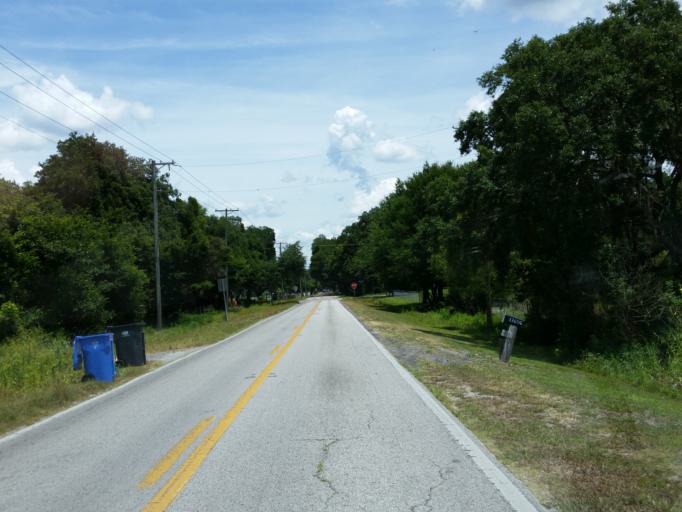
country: US
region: Florida
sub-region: Hillsborough County
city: Dover
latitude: 28.0471
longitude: -82.2175
